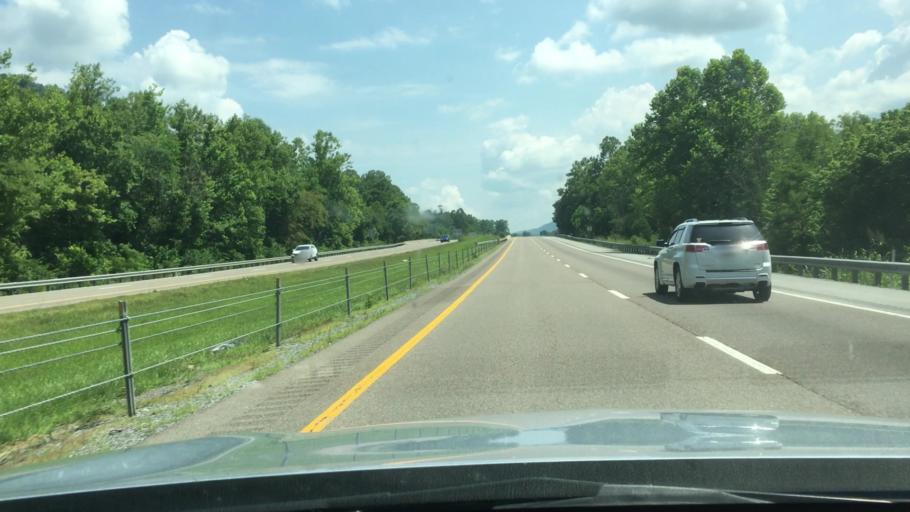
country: US
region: Tennessee
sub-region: Unicoi County
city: Erwin
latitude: 36.1583
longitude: -82.4084
